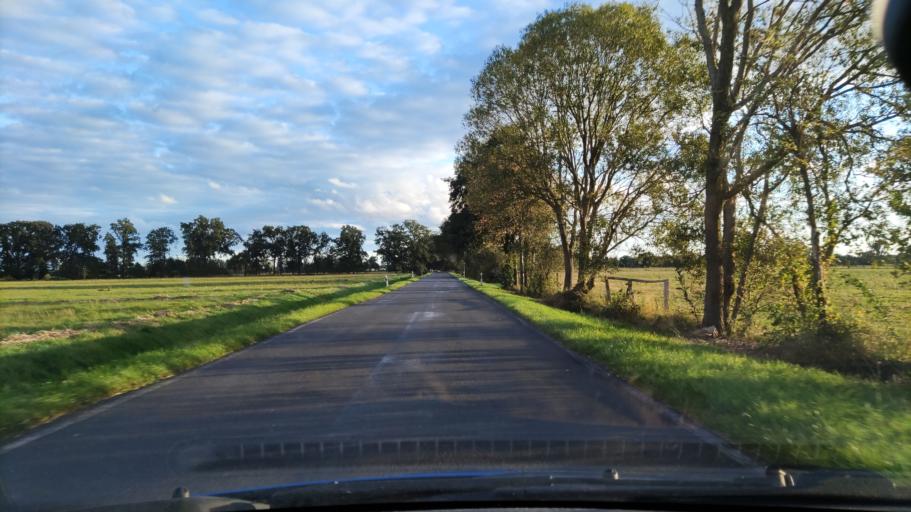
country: DE
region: Lower Saxony
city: Neu Darchau
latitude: 53.3606
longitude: 10.8649
